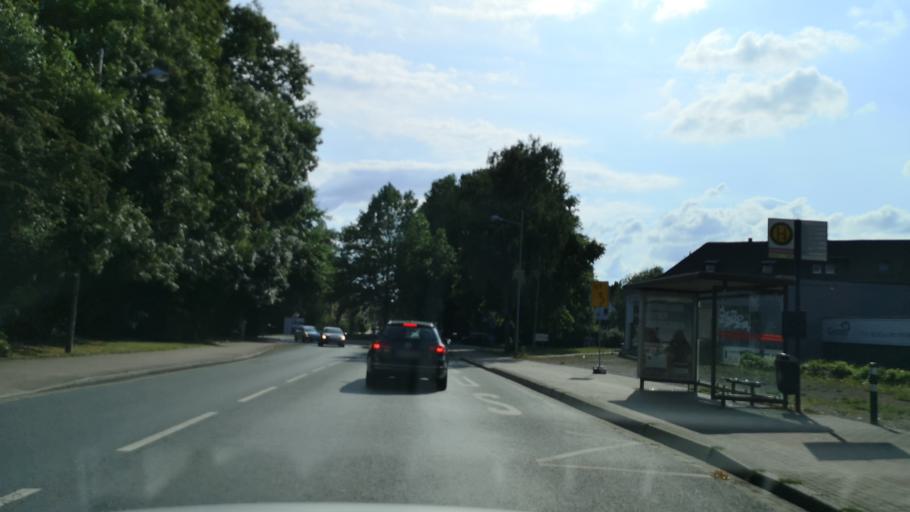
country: DE
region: North Rhine-Westphalia
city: Schwerte
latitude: 51.4463
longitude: 7.5808
